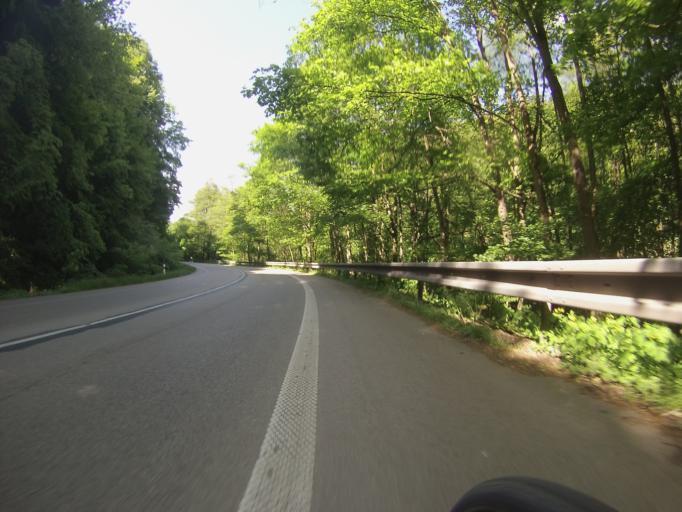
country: CZ
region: South Moravian
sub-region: Okres Blansko
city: Blansko
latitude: 49.3357
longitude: 16.6488
